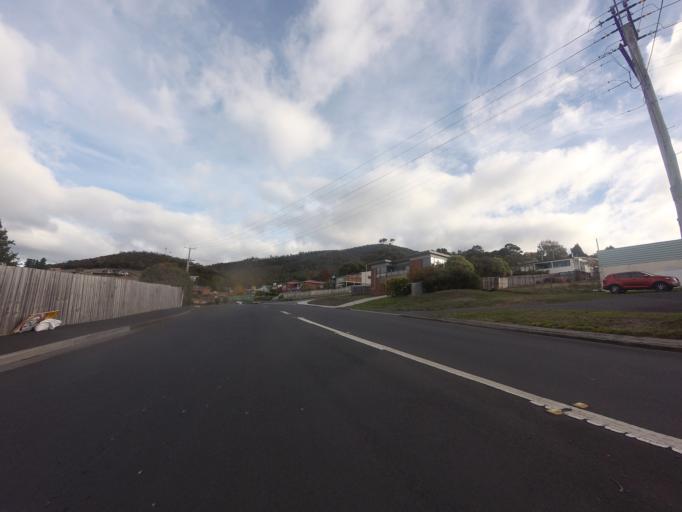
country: AU
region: Tasmania
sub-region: Glenorchy
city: Berriedale
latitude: -42.8148
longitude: 147.2404
